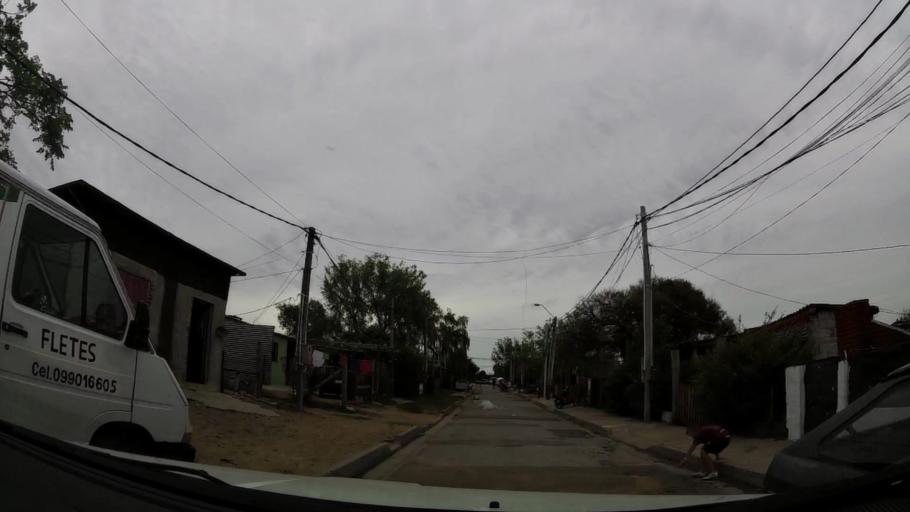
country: UY
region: Maldonado
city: Maldonado
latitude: -34.8955
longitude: -54.9353
